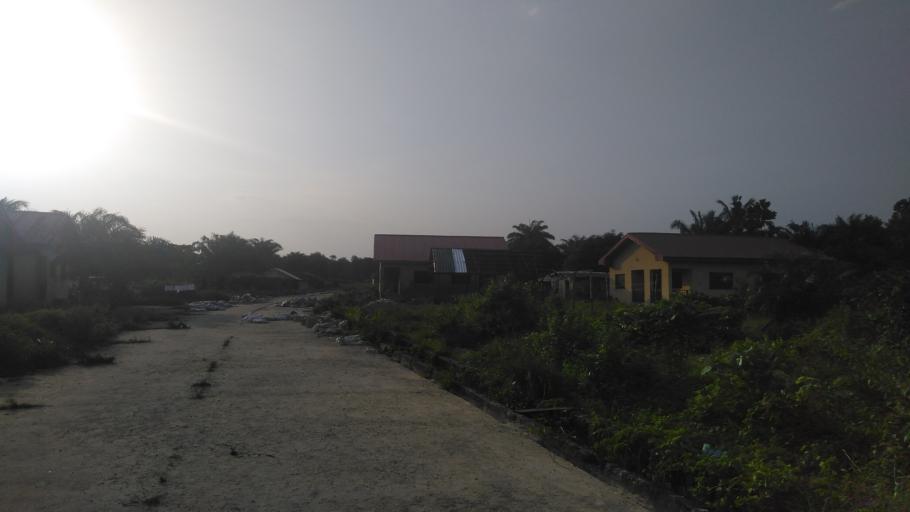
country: NG
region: Delta
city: Sapele
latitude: 5.8400
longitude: 5.1227
